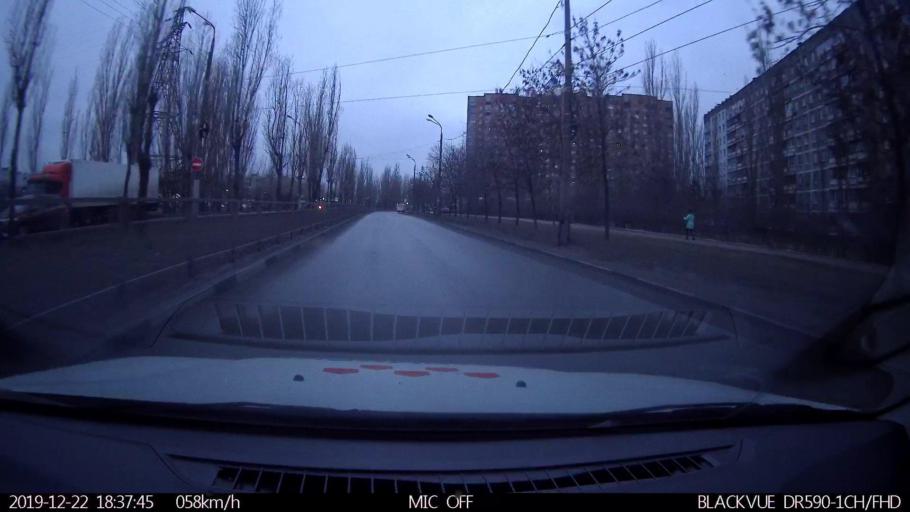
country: RU
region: Nizjnij Novgorod
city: Nizhniy Novgorod
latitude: 56.3318
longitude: 43.9378
